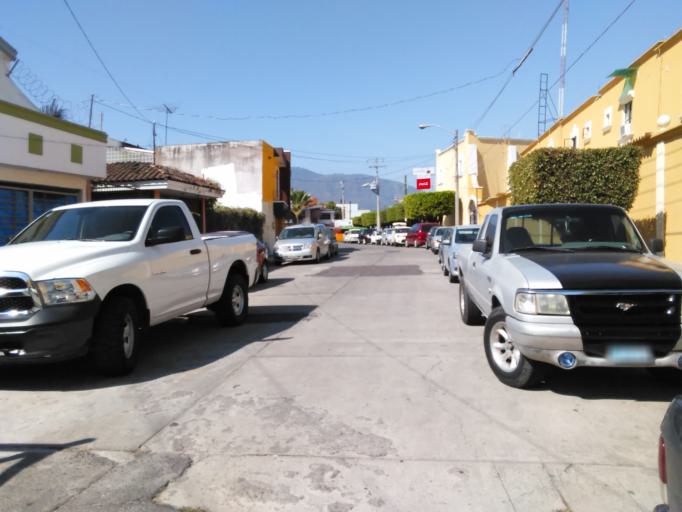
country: MX
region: Nayarit
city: Tepic
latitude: 21.4868
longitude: -104.8847
